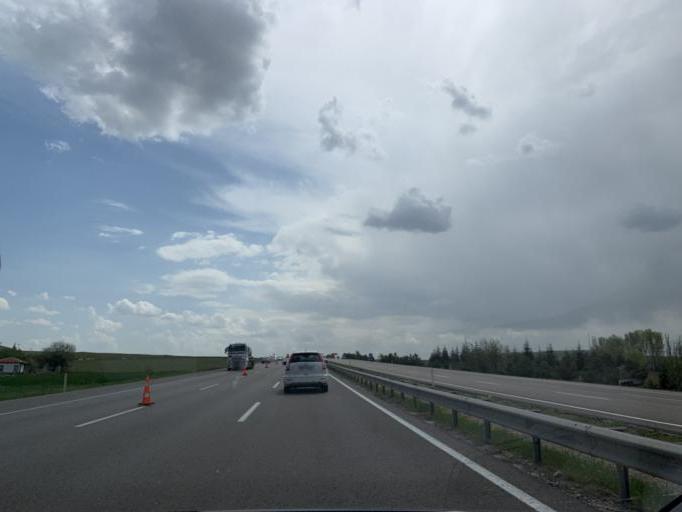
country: TR
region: Ankara
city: Polatli
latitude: 39.6233
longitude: 32.1916
